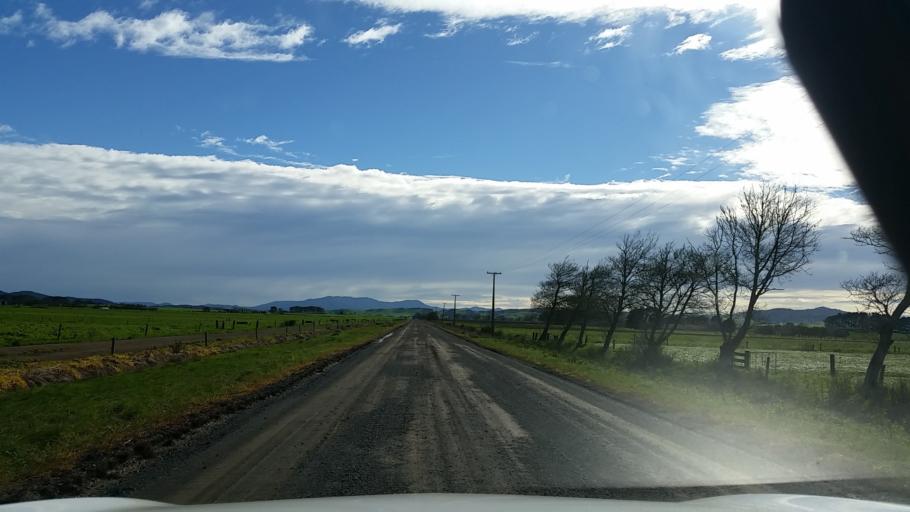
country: NZ
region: Waikato
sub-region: Hamilton City
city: Hamilton
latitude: -37.6422
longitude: 175.4317
